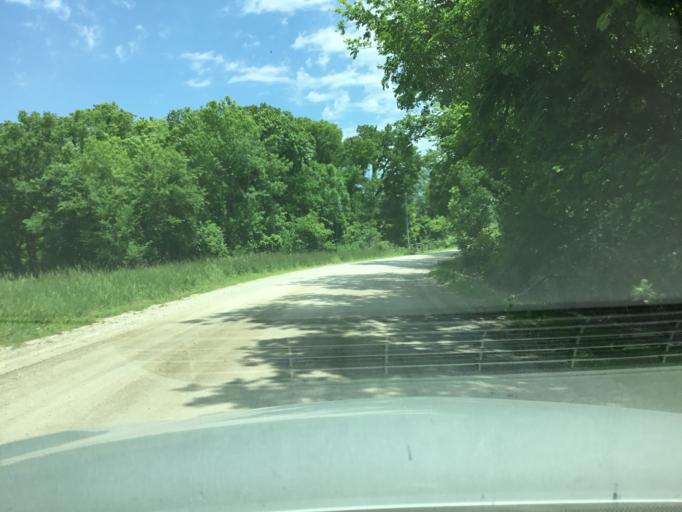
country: US
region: Kansas
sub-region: Montgomery County
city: Independence
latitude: 37.1094
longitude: -95.7818
